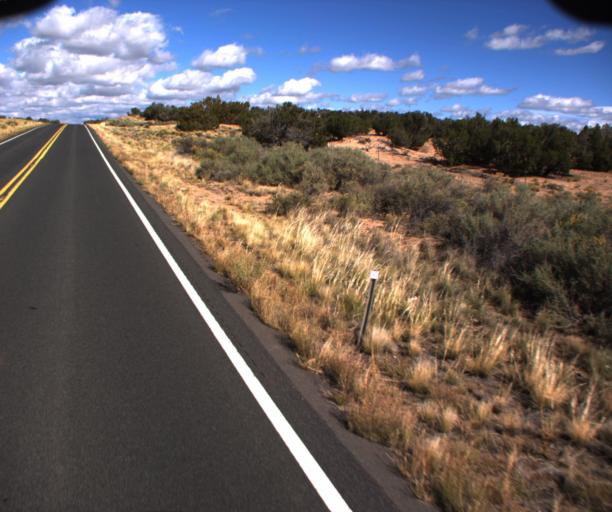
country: US
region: Arizona
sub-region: Apache County
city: Houck
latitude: 35.1011
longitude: -109.3141
